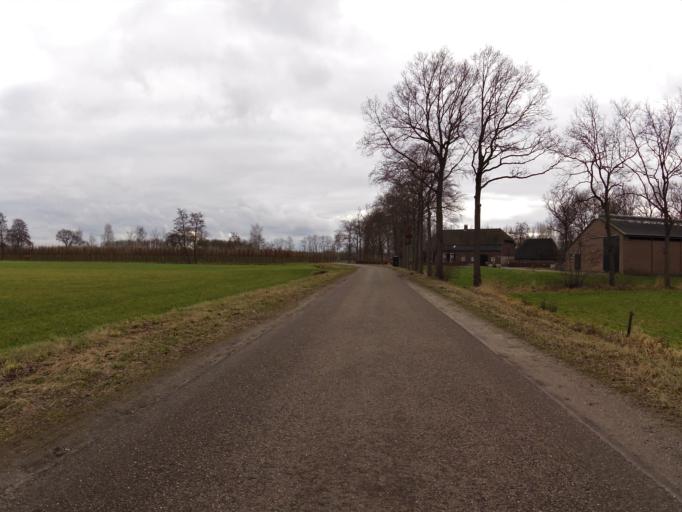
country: NL
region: North Brabant
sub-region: Gemeente Boxtel
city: Boxtel
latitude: 51.5965
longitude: 5.2818
